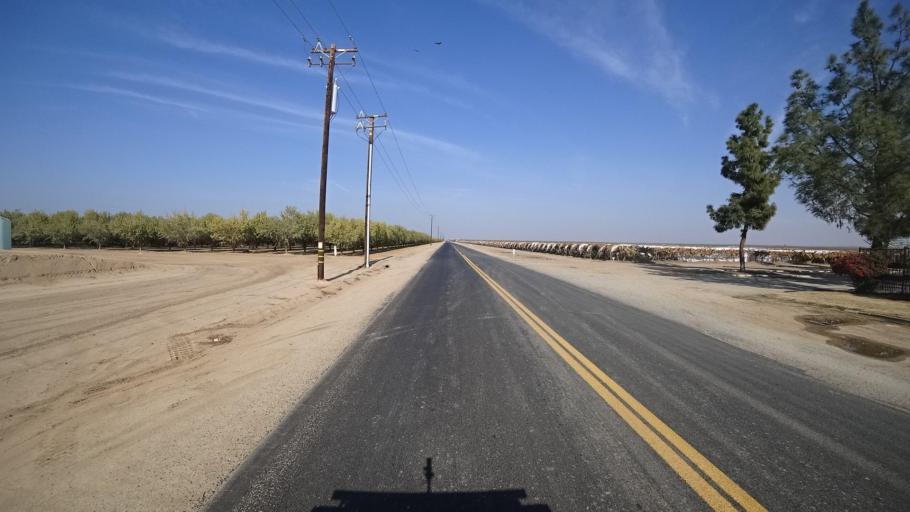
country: US
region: California
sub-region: Kern County
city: Shafter
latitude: 35.5066
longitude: -119.1523
